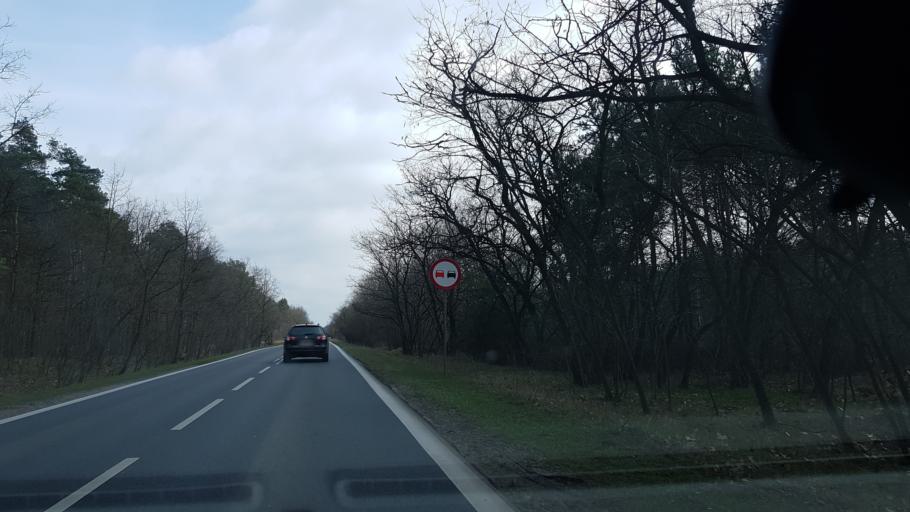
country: PL
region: Masovian Voivodeship
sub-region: Warszawa
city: Wesola
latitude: 52.2554
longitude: 21.2058
